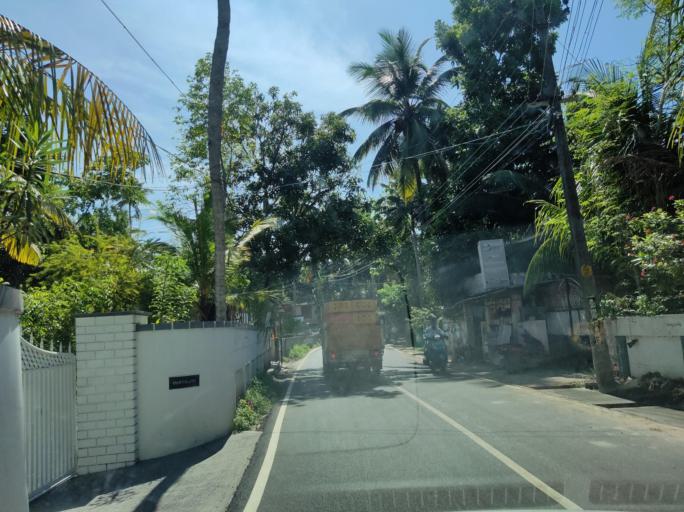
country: IN
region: Kerala
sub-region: Alappuzha
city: Kayankulam
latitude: 9.2657
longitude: 76.4063
